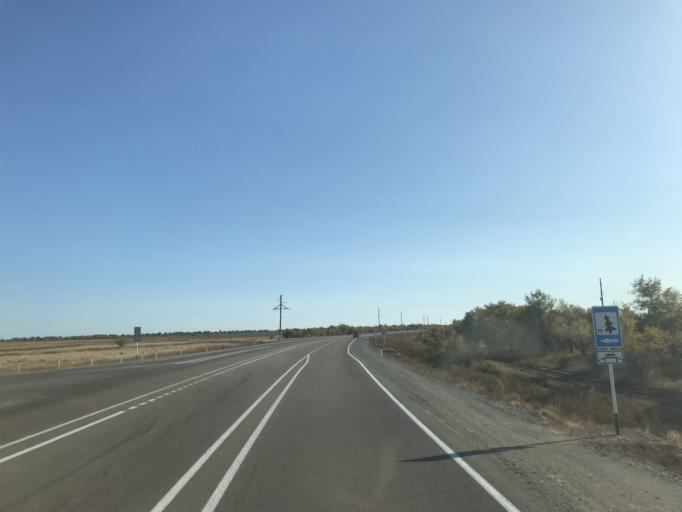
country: KZ
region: Pavlodar
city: Koktobe
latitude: 51.7279
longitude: 77.5596
